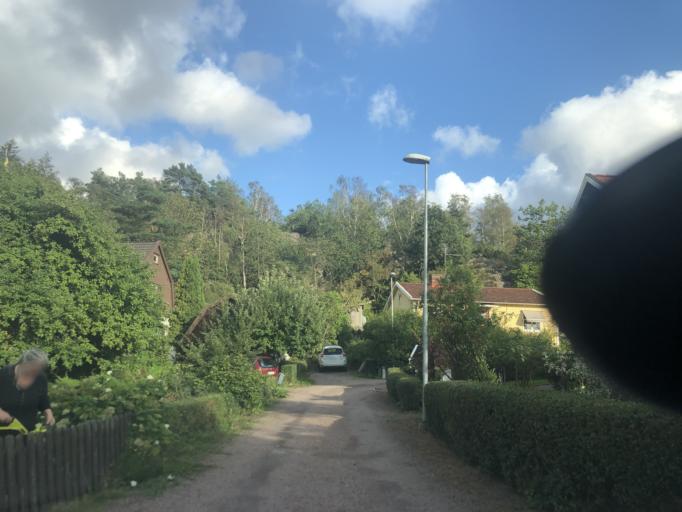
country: SE
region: Vaestra Goetaland
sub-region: Goteborg
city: Goeteborg
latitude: 57.7436
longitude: 11.9591
